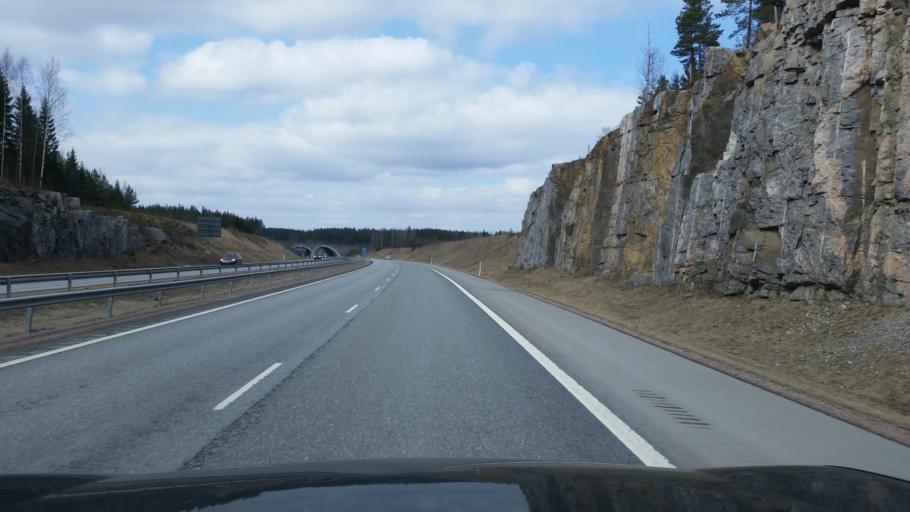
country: FI
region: Uusimaa
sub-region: Helsinki
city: Sammatti
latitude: 60.3747
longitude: 23.8287
